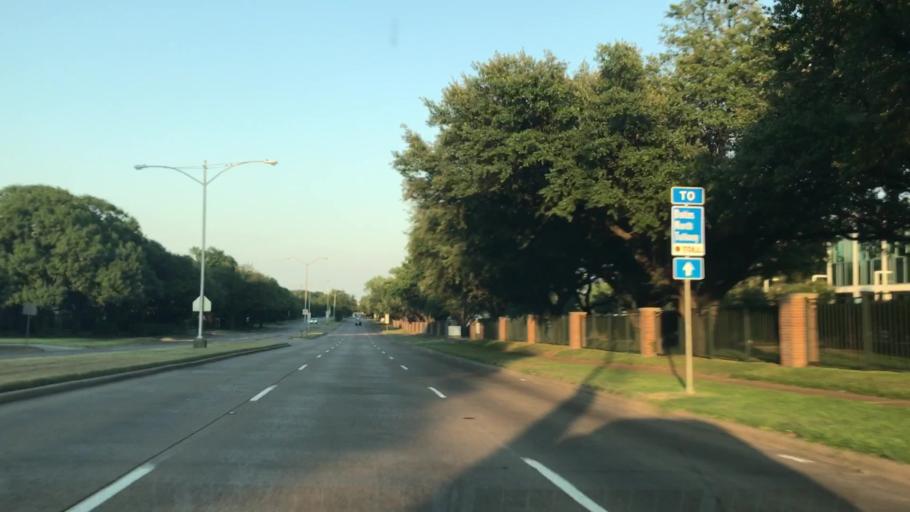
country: US
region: Texas
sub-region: Dallas County
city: Addison
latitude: 32.9095
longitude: -96.8288
